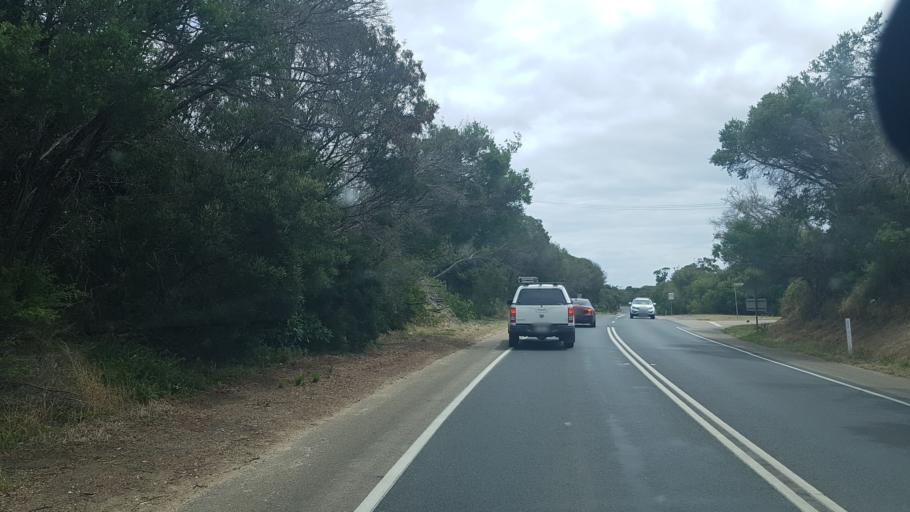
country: AU
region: Victoria
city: Rye
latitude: -38.3793
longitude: 144.8043
